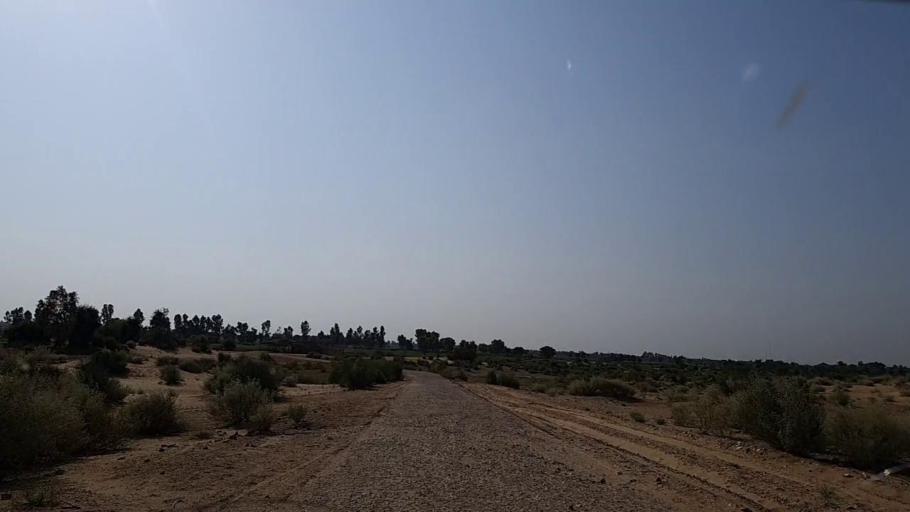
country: PK
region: Sindh
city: Khanpur
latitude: 27.7370
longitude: 69.3723
